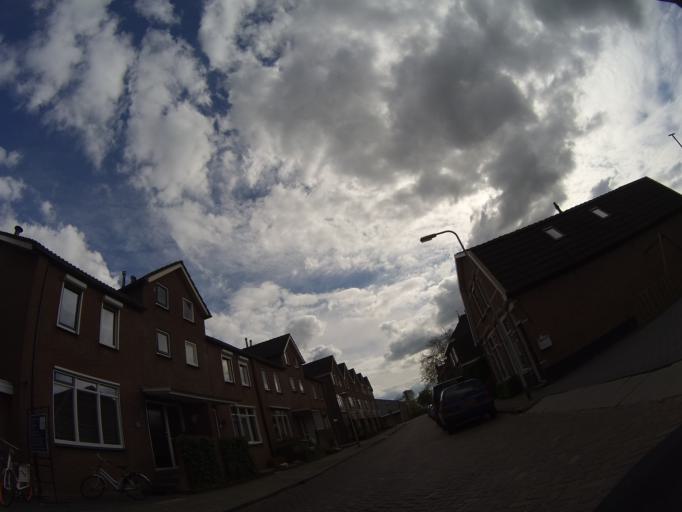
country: NL
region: Drenthe
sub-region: Gemeente Coevorden
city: Coevorden
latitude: 52.6599
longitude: 6.7395
